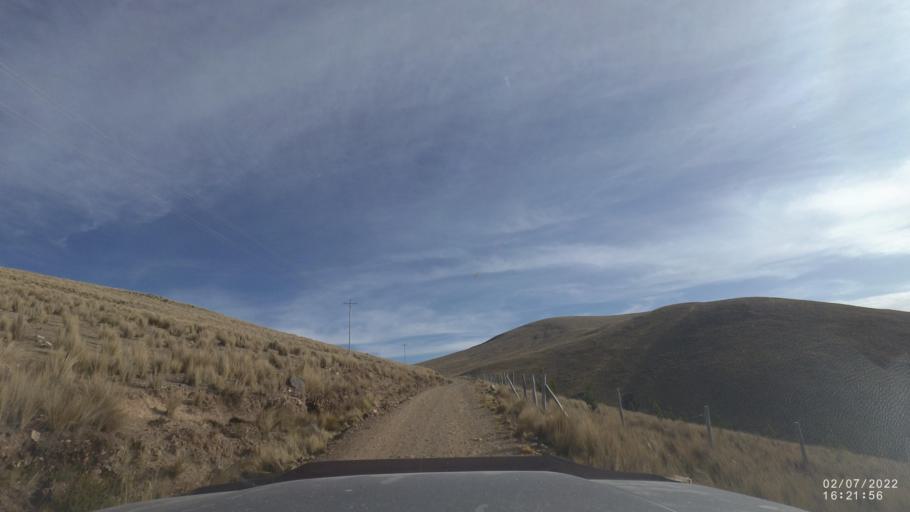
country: BO
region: Cochabamba
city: Irpa Irpa
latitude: -17.9327
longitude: -66.4539
